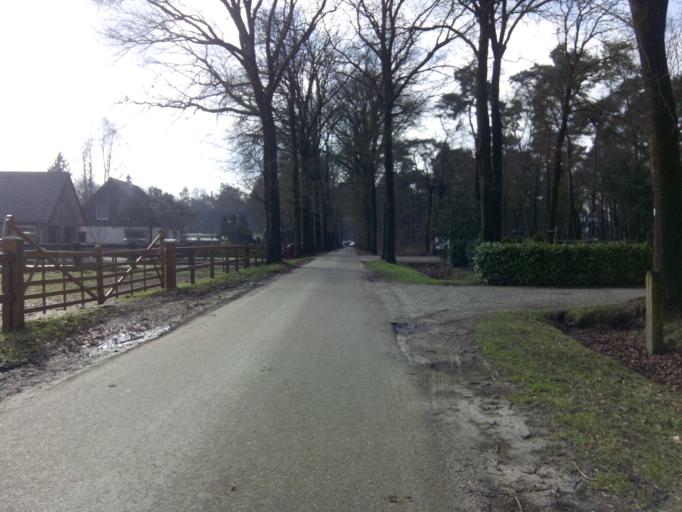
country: NL
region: Utrecht
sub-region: Gemeente Utrechtse Heuvelrug
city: Leersum
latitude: 52.0454
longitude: 5.4502
